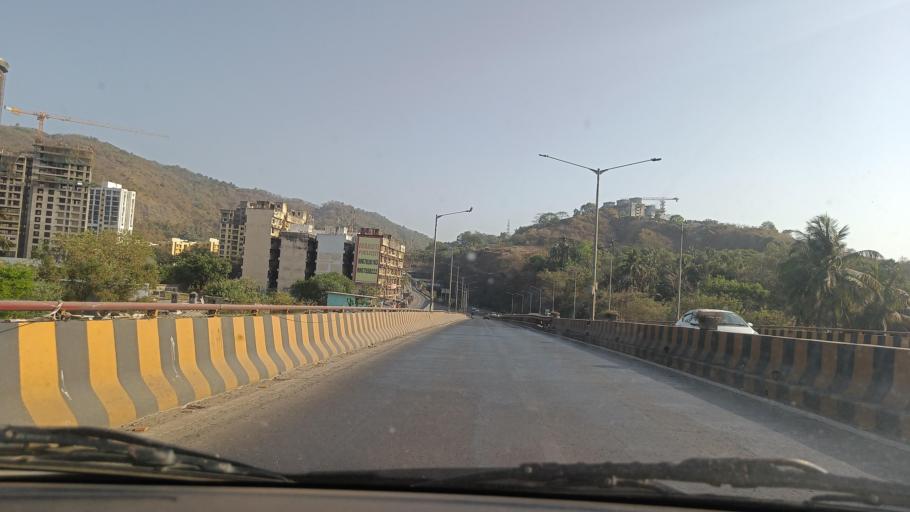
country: IN
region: Maharashtra
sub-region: Mumbai Suburban
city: Mumbai
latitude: 19.0430
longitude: 72.9088
